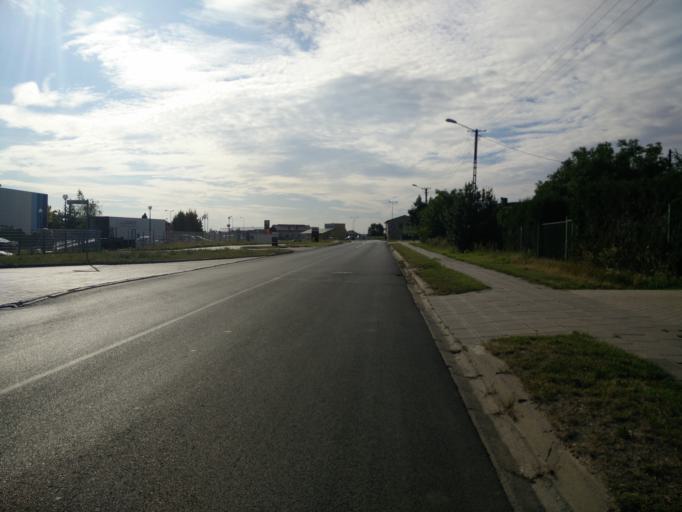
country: PL
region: Greater Poland Voivodeship
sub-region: Powiat sredzki
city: Sroda Wielkopolska
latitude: 52.2314
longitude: 17.2554
